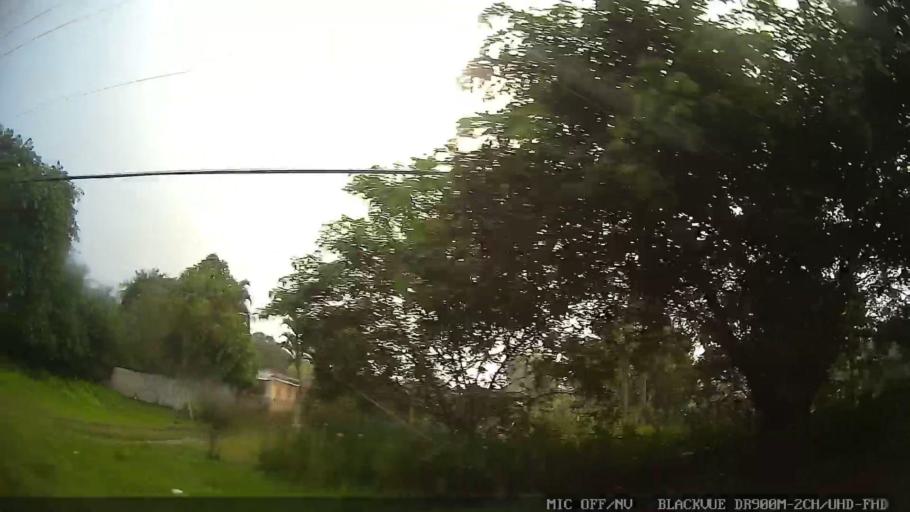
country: BR
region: Sao Paulo
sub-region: Itanhaem
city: Itanhaem
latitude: -24.1231
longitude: -46.7831
